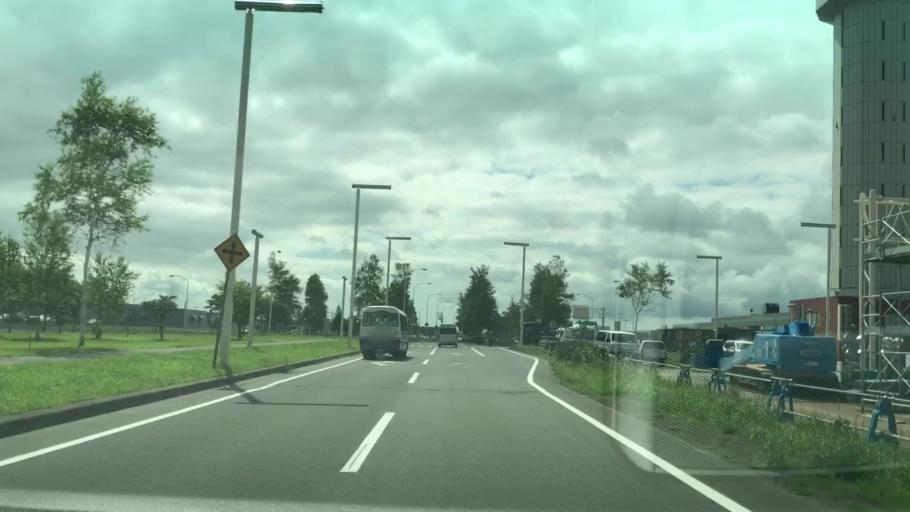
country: JP
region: Hokkaido
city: Chitose
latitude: 42.7842
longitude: 141.6774
